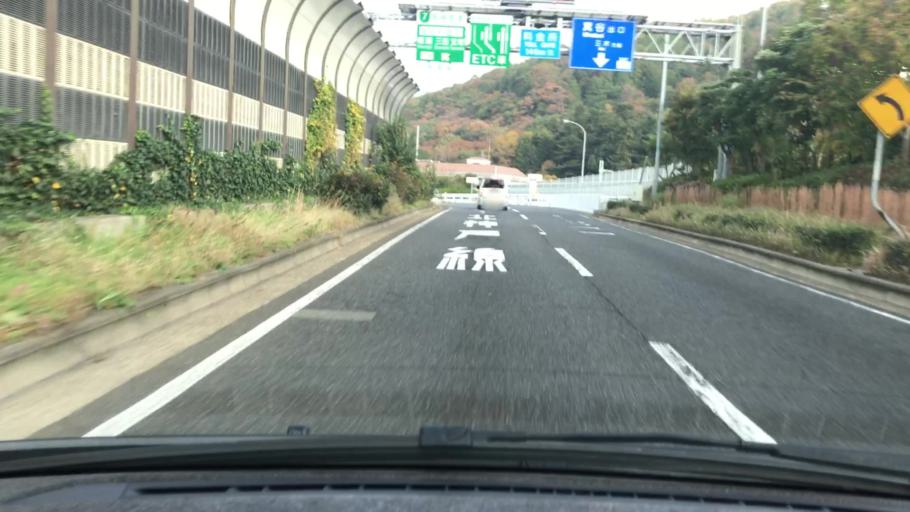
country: JP
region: Hyogo
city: Kobe
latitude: 34.7605
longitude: 135.1588
